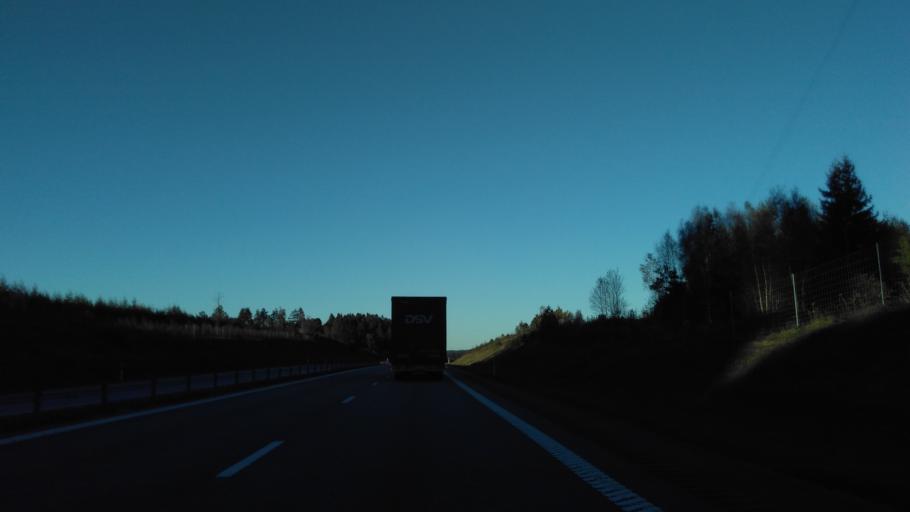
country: SE
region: Vaestra Goetaland
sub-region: Boras Kommun
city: Dalsjofors
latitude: 57.7756
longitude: 13.1162
